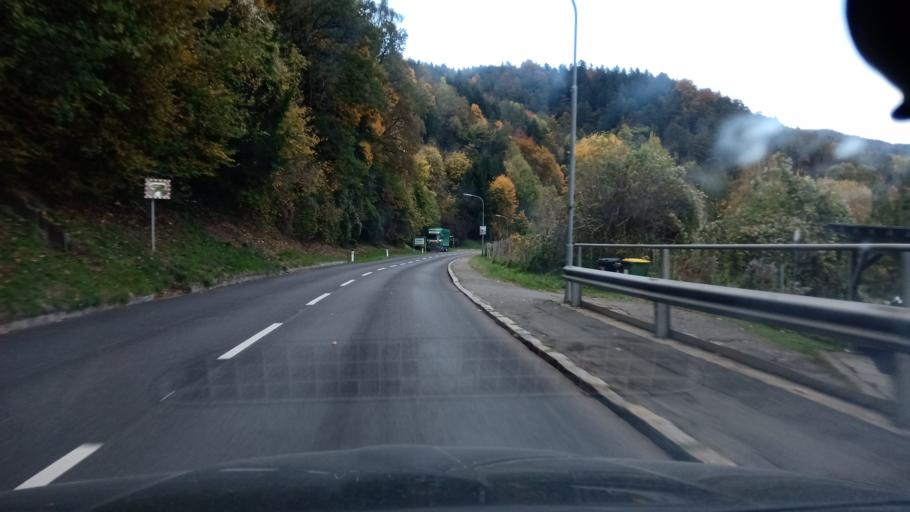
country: AT
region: Styria
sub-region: Politischer Bezirk Leoben
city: Proleb
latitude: 47.3917
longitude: 15.1238
